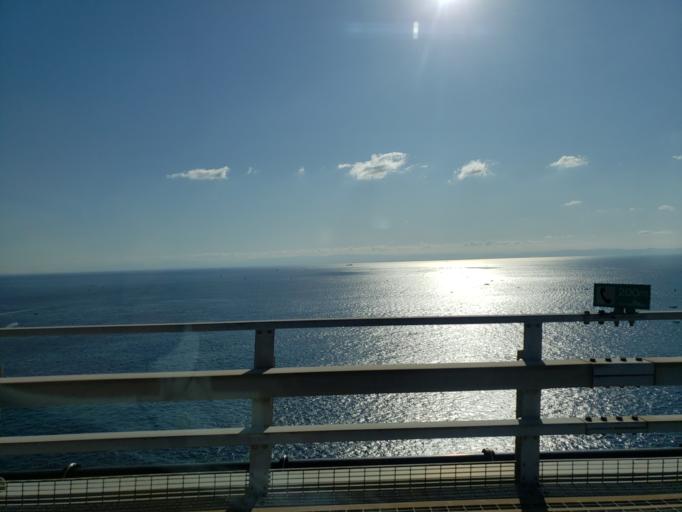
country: JP
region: Hyogo
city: Akashi
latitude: 34.6149
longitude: 135.0194
